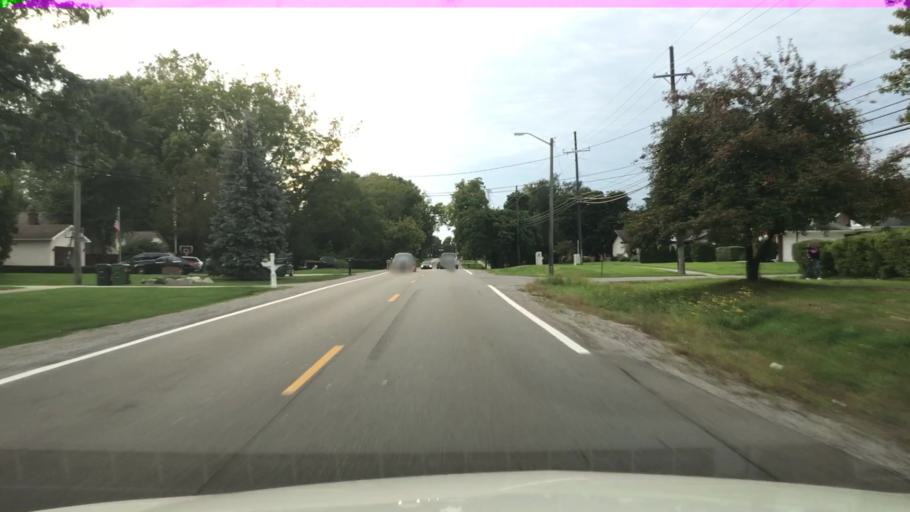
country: US
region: Michigan
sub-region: Macomb County
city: Shelby
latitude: 42.6828
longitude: -83.0786
